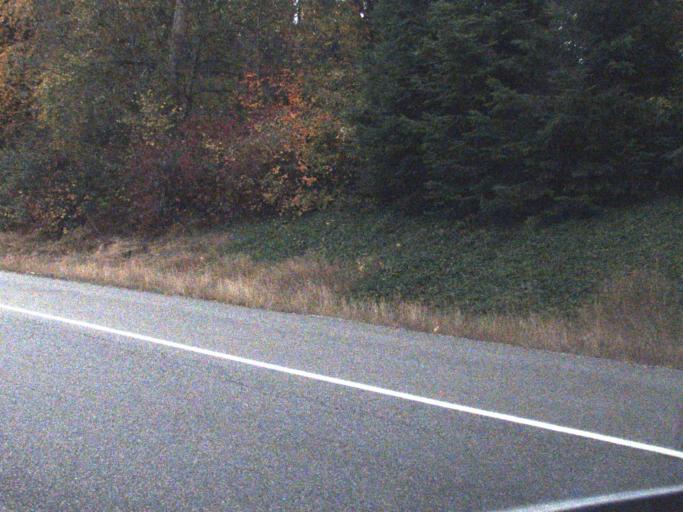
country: US
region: Washington
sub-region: Snohomish County
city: Alderwood Manor
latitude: 47.8445
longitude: -122.2743
